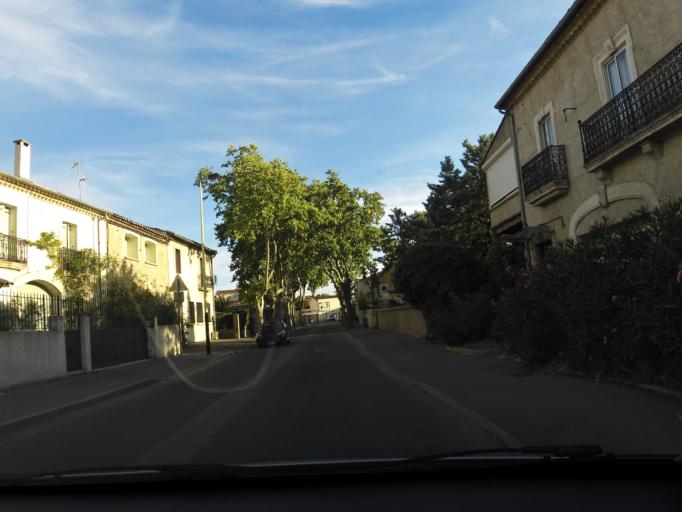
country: FR
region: Languedoc-Roussillon
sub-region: Departement de l'Herault
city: Prades-le-Lez
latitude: 43.7003
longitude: 3.8625
